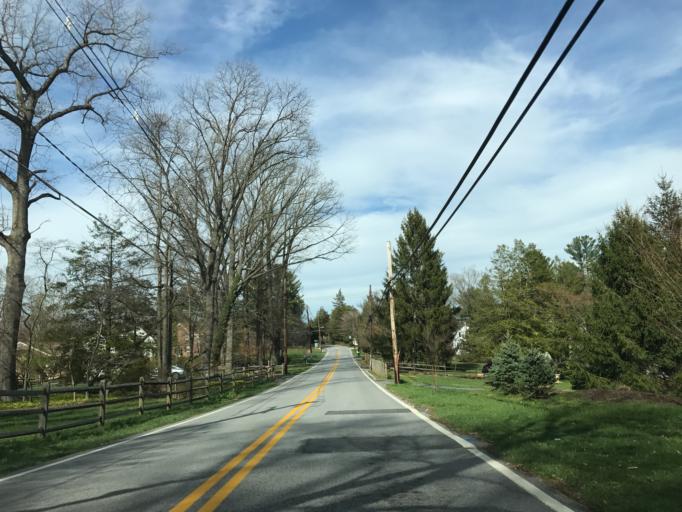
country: US
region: Maryland
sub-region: Baltimore County
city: Hampton
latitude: 39.4243
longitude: -76.5623
